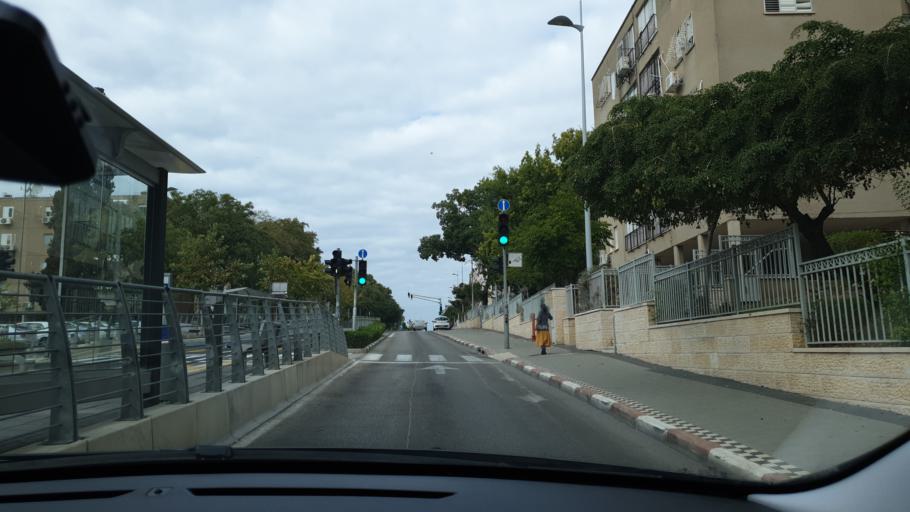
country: IL
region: Haifa
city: Qiryat Ata
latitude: 32.8082
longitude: 35.1175
